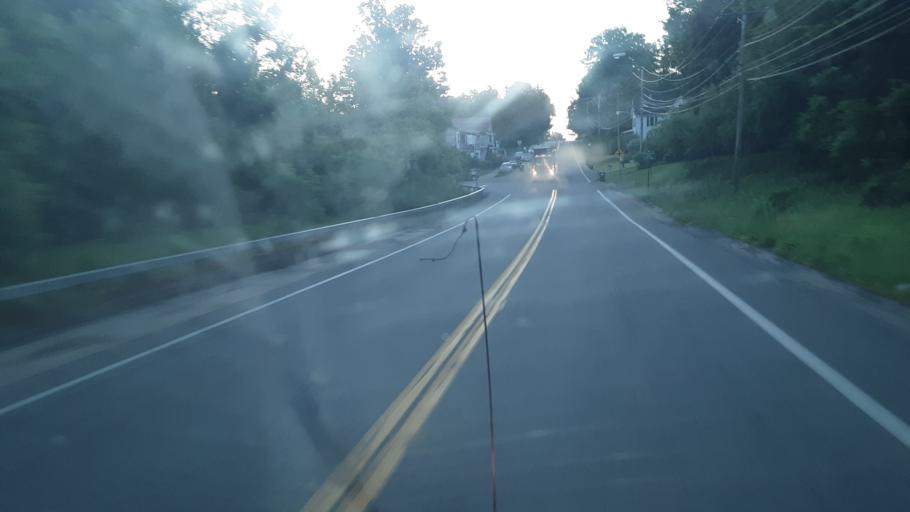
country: US
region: New York
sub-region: Saratoga County
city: Ballston Spa
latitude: 43.0001
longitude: -73.8575
